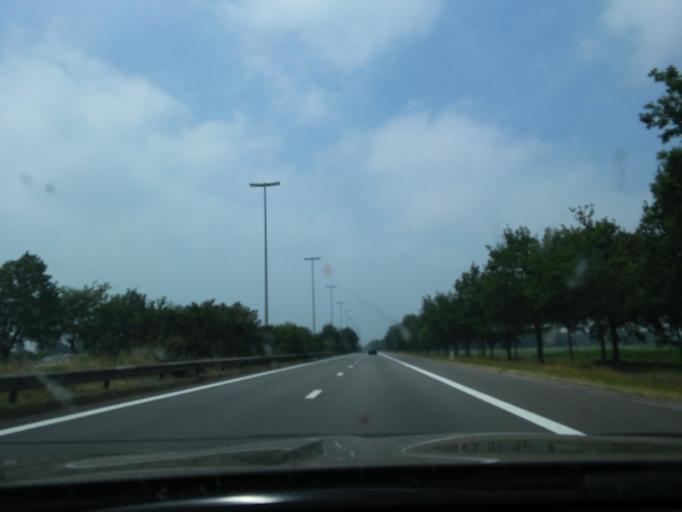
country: BE
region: Flanders
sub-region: Provincie Oost-Vlaanderen
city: Stekene
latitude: 51.2172
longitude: 4.0118
